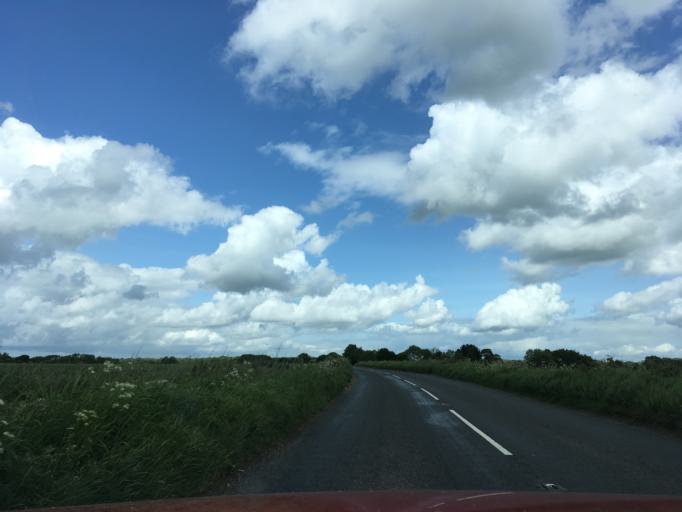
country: GB
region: England
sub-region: Gloucestershire
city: Shurdington
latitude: 51.7959
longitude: -2.1269
